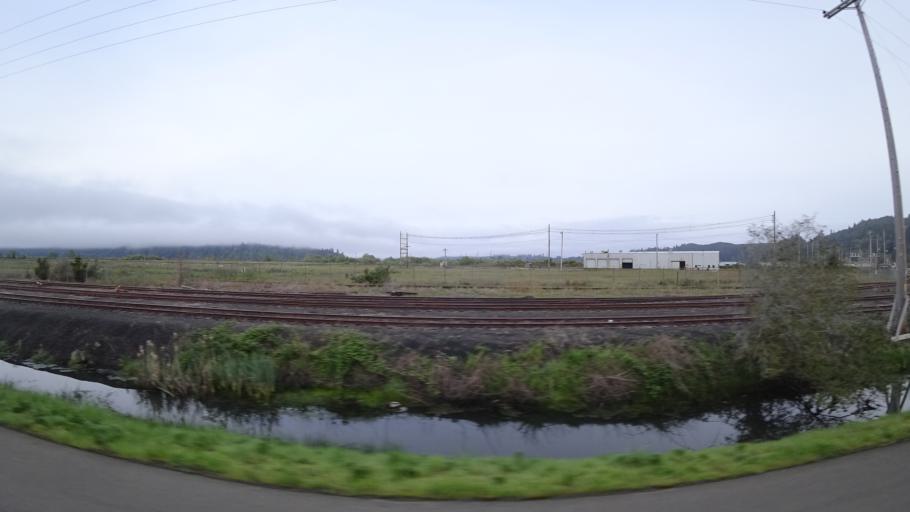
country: US
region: Oregon
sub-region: Douglas County
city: Reedsport
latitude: 43.7392
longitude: -124.1111
